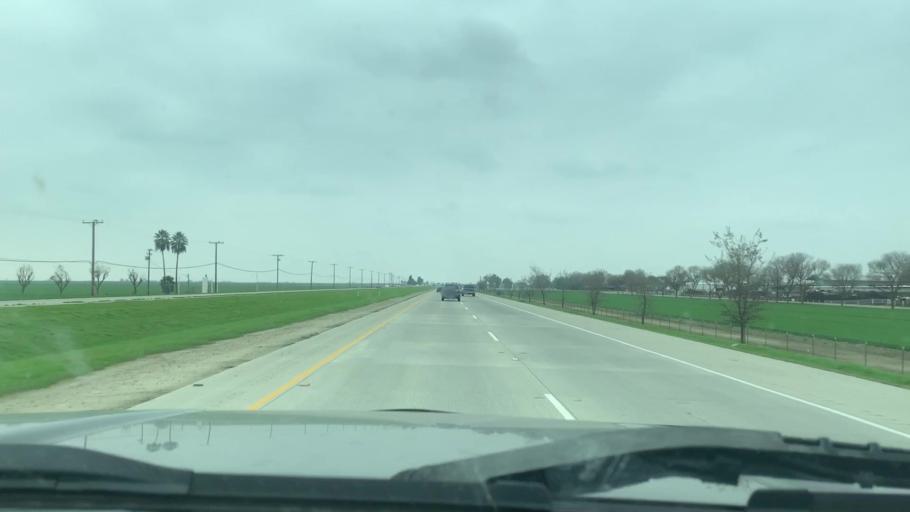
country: US
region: California
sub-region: Tulare County
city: Goshen
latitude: 36.3286
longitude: -119.5211
